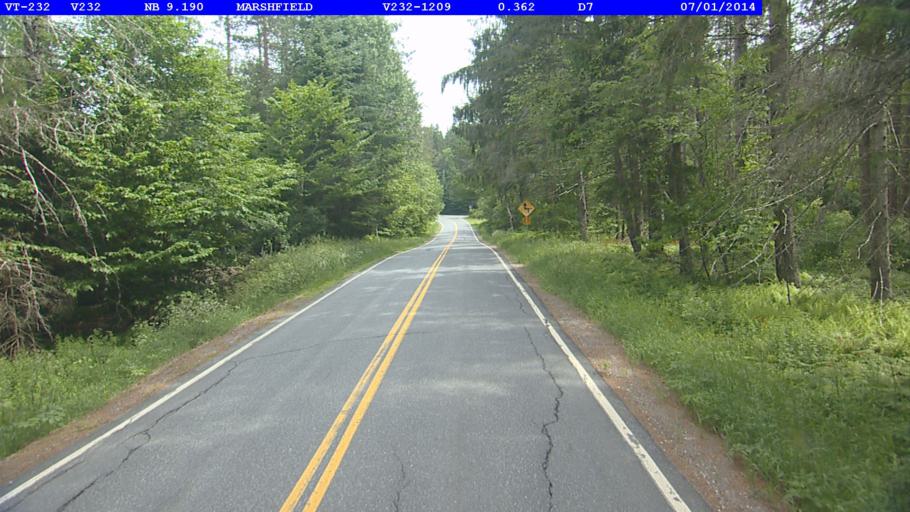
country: US
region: Vermont
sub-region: Caledonia County
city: Hardwick
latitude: 44.3215
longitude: -72.2910
